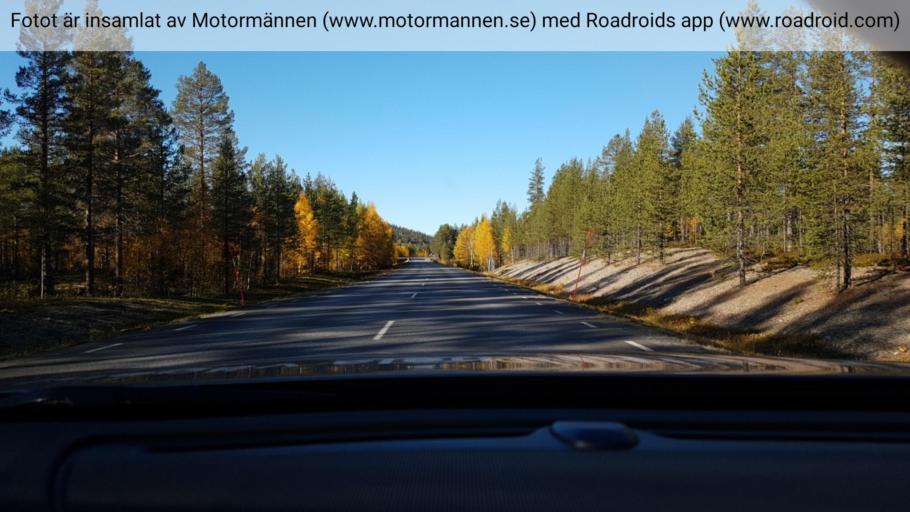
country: SE
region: Vaesterbotten
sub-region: Norsjo Kommun
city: Norsjoe
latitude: 65.4111
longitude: 19.7066
